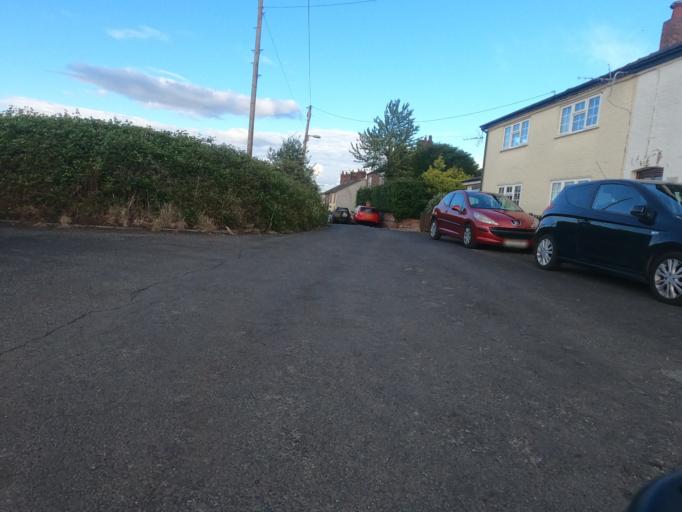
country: GB
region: England
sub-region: Cheshire West and Chester
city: Hartford
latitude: 53.2242
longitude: -2.5240
